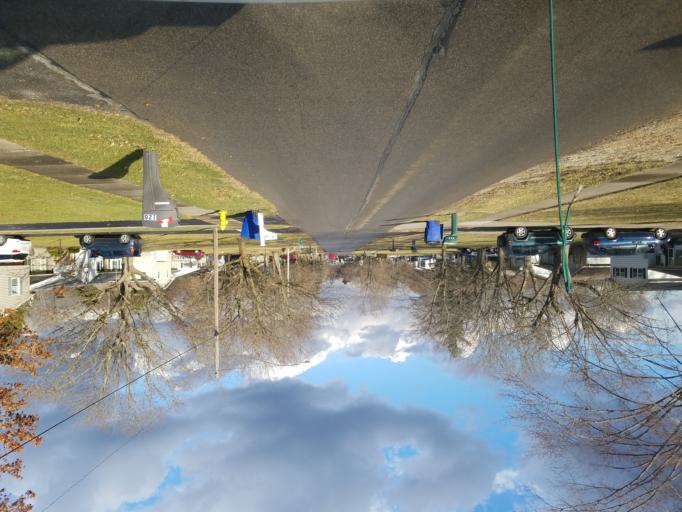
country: US
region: Ohio
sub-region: Delaware County
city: Delaware
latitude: 40.3103
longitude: -83.0916
